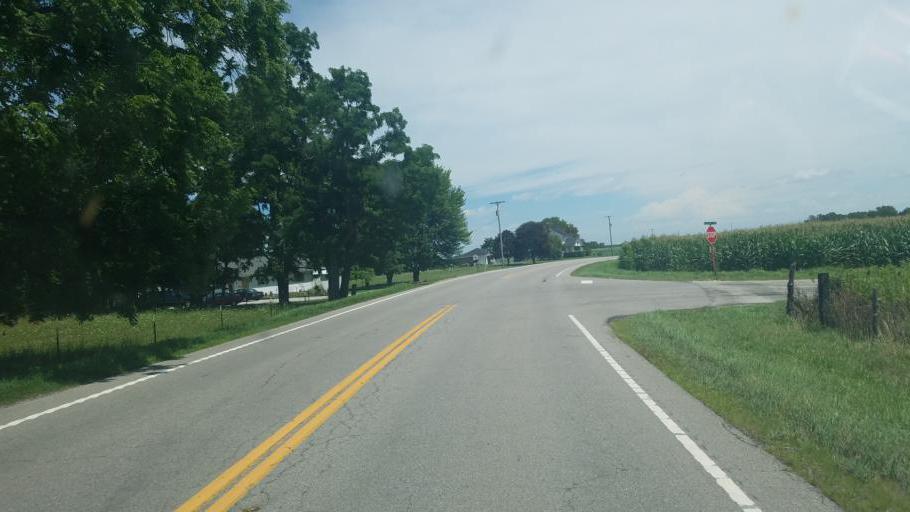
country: US
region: Ohio
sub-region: Richland County
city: Shelby
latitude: 40.8930
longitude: -82.5719
